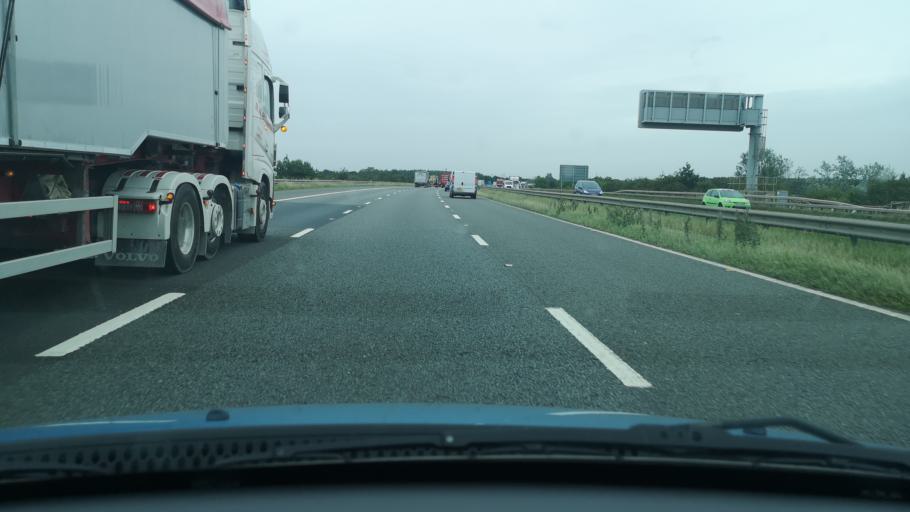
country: GB
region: England
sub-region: Doncaster
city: Hatfield
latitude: 53.6013
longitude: -0.9910
